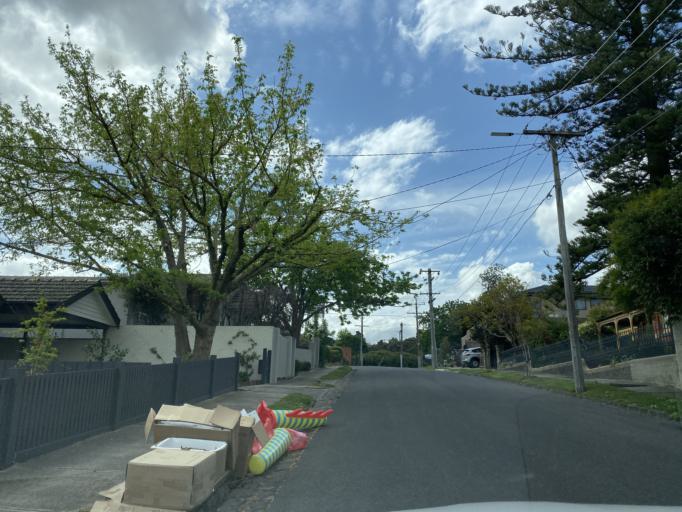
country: AU
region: Victoria
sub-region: Whitehorse
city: Surrey Hills
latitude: -37.8307
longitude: 145.1064
